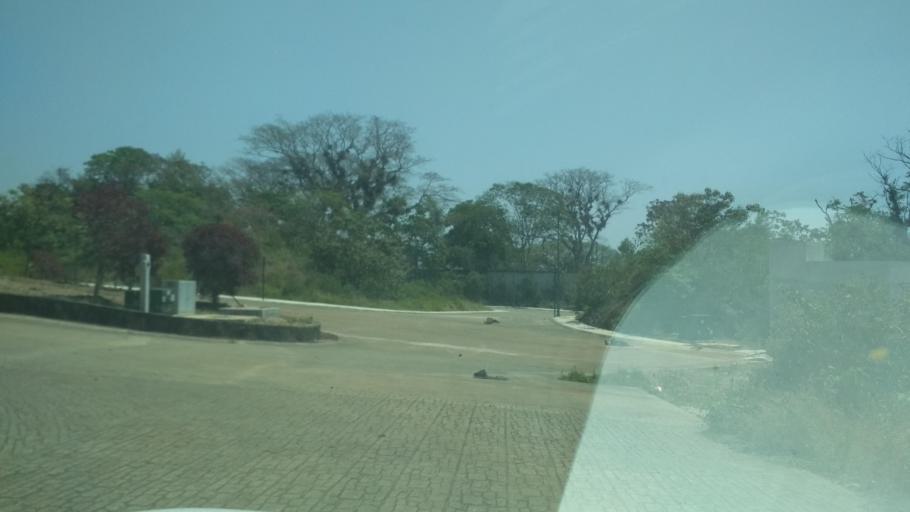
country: MX
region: Veracruz
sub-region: Emiliano Zapata
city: Las Trancas
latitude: 19.5246
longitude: -96.8742
